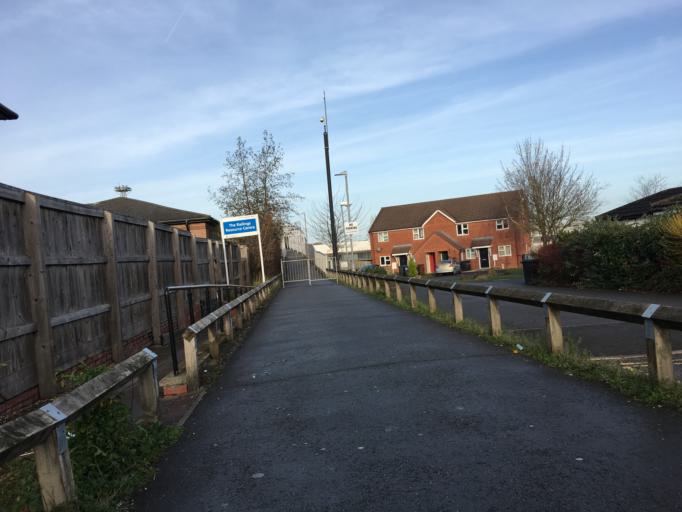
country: GB
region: England
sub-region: Warwickshire
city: Rugby
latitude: 52.3791
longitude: -1.2587
